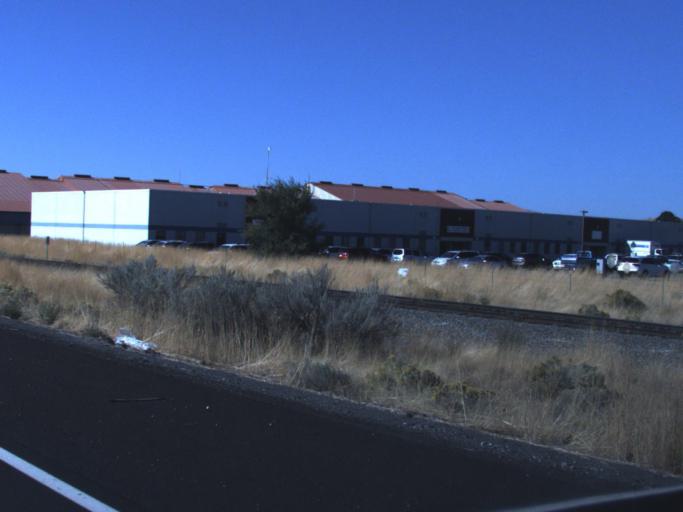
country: US
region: Washington
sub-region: Benton County
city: Richland
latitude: 46.2968
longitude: -119.3017
